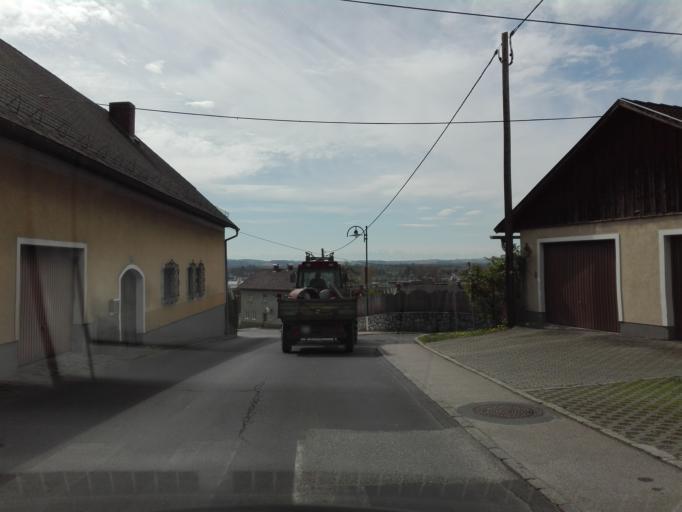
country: AT
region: Upper Austria
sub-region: Politischer Bezirk Urfahr-Umgebung
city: Walding
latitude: 48.3517
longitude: 14.1597
